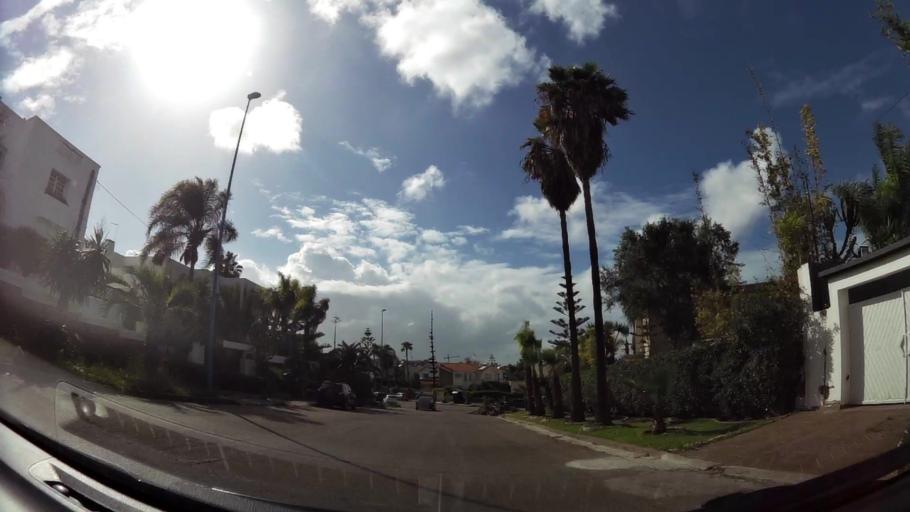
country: MA
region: Grand Casablanca
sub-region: Casablanca
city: Casablanca
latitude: 33.5499
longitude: -7.6293
